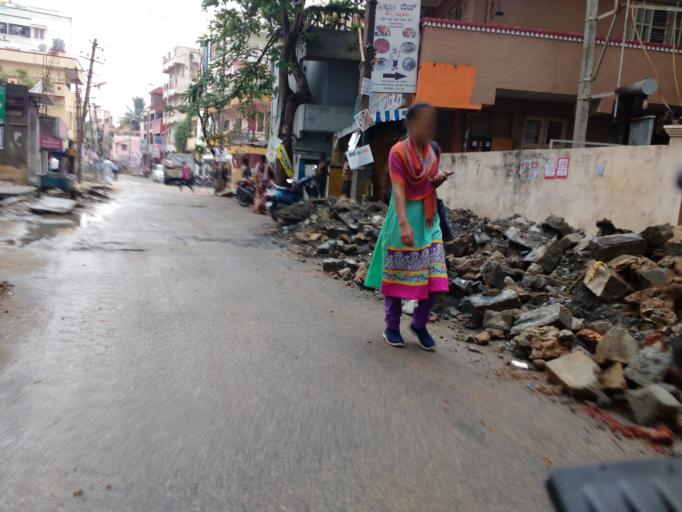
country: IN
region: Karnataka
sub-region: Bangalore Urban
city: Bangalore
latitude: 12.9940
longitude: 77.6664
